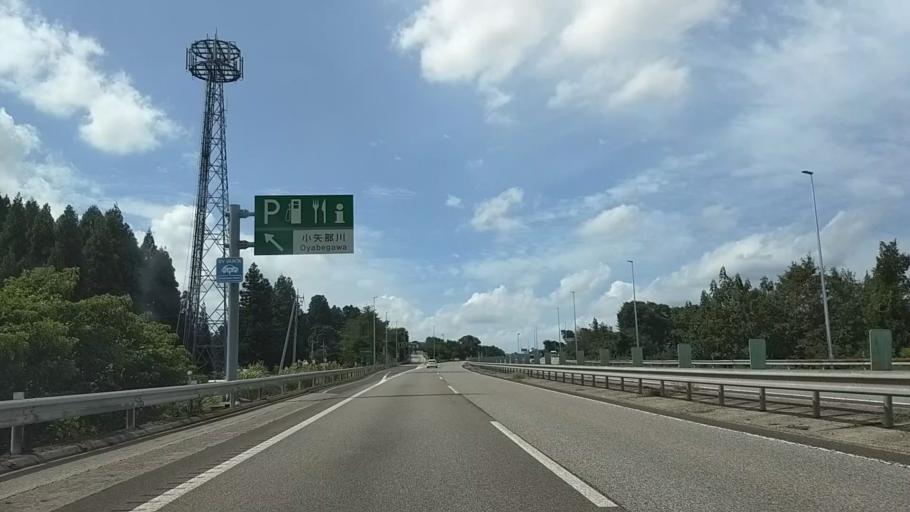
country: JP
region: Toyama
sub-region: Oyabe Shi
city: Oyabe
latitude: 36.6274
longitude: 136.8780
